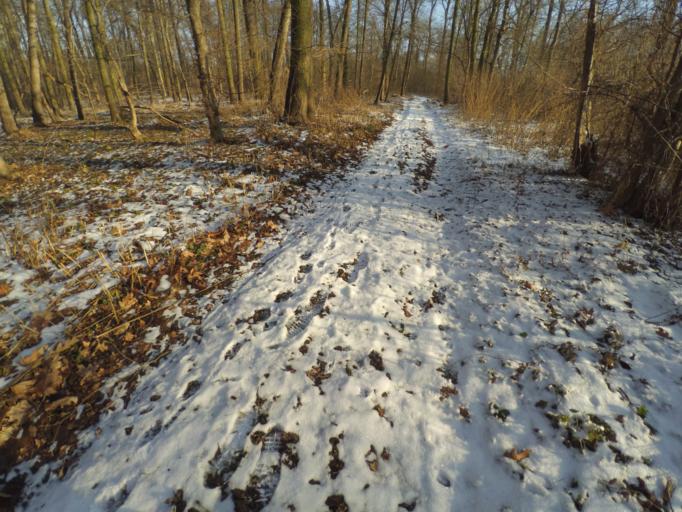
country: CZ
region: Central Bohemia
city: Libis
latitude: 50.2864
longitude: 14.5152
